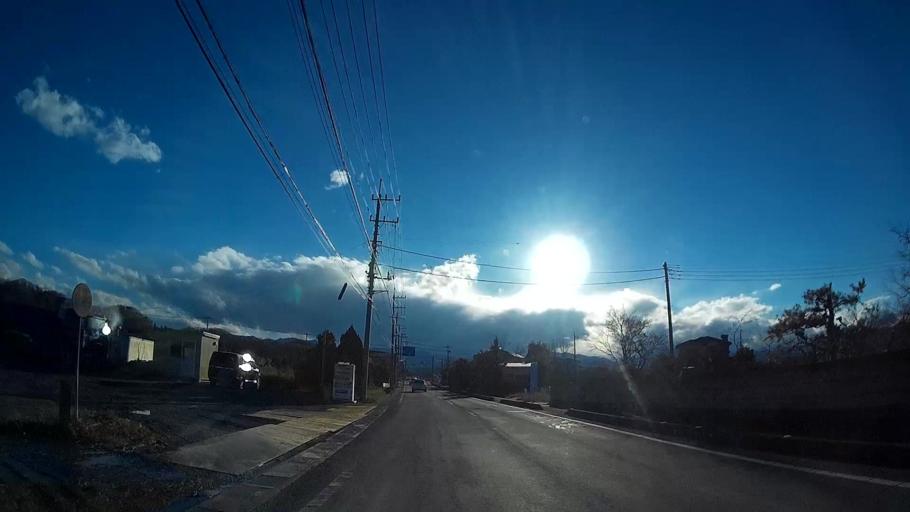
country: JP
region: Saitama
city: Chichibu
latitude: 36.0629
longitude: 139.0845
